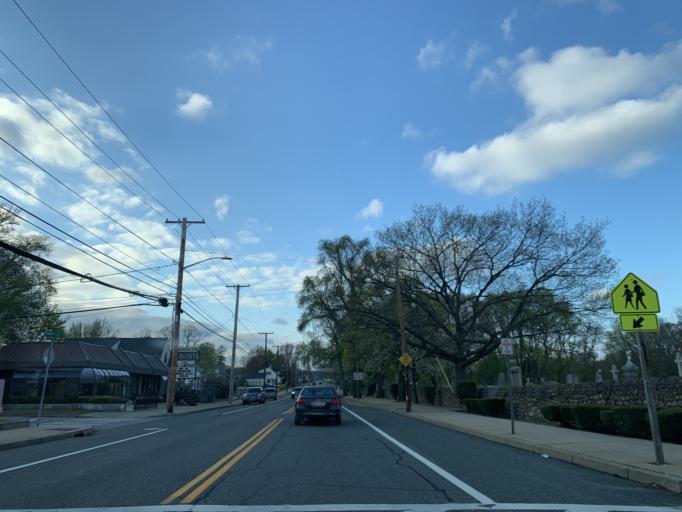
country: US
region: Rhode Island
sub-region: Providence County
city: Pawtucket
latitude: 41.8638
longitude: -71.4121
